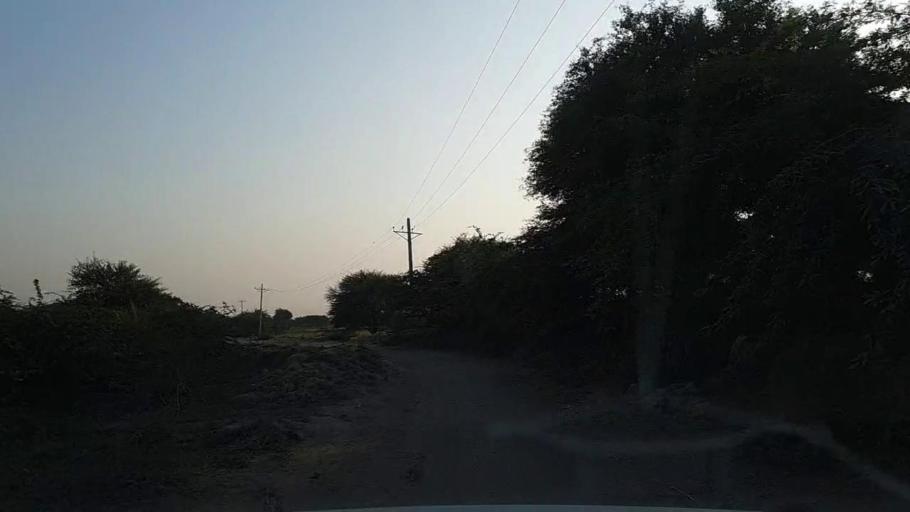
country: PK
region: Sindh
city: Daro Mehar
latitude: 24.7292
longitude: 68.1804
